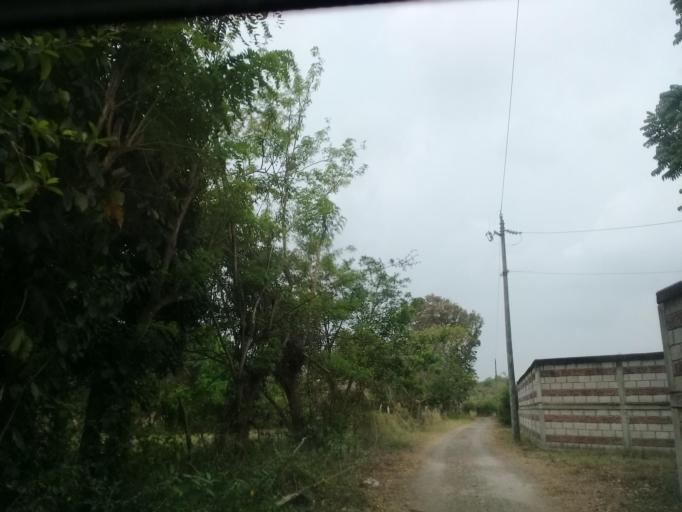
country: MX
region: Veracruz
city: Jamapa
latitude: 19.0500
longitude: -96.1991
